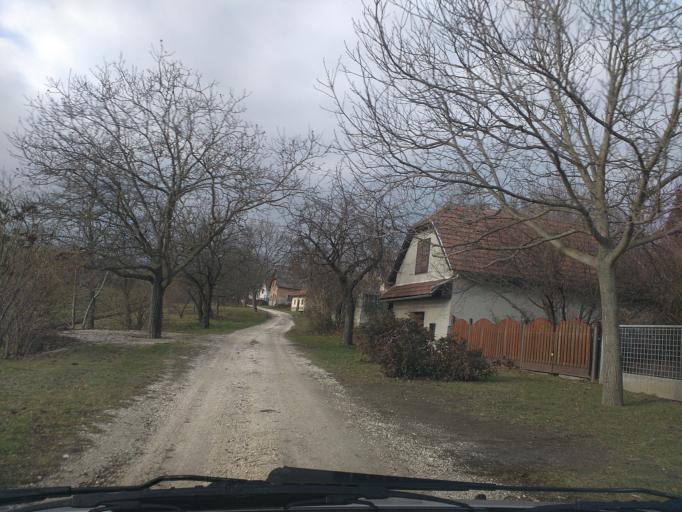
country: HU
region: Komarom-Esztergom
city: Piliscsev
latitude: 47.6847
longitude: 18.8326
